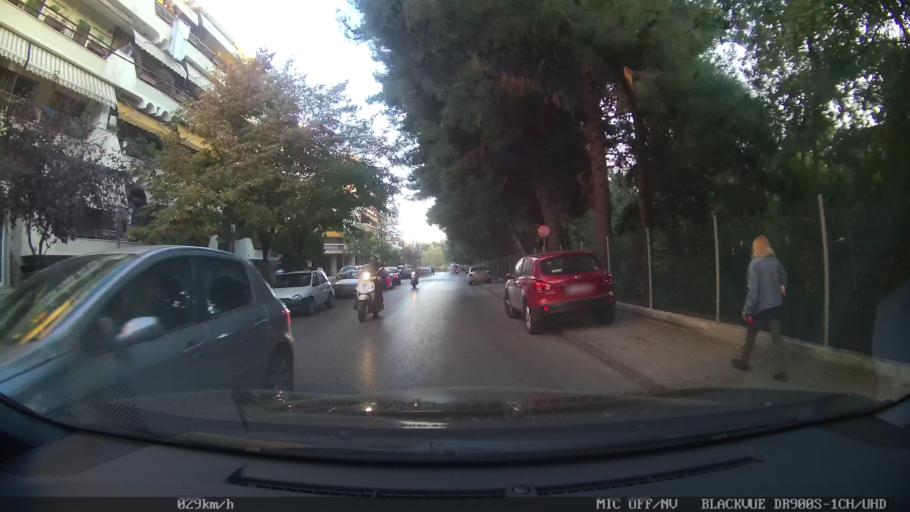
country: GR
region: Central Macedonia
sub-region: Nomos Thessalonikis
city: Pylaia
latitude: 40.6063
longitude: 22.9833
